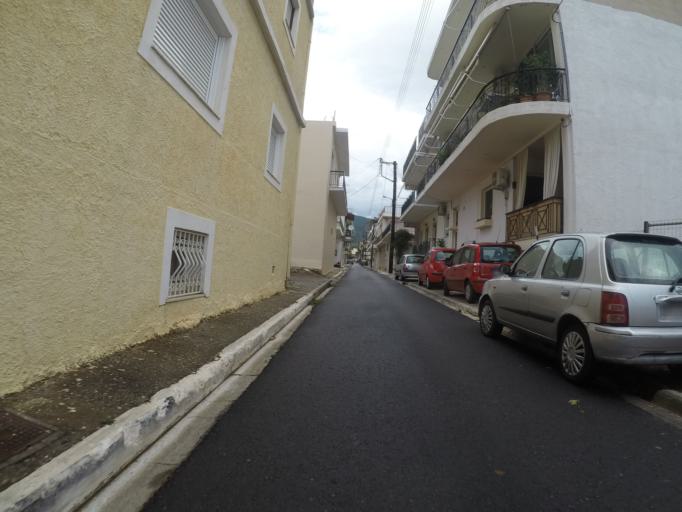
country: GR
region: Peloponnese
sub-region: Nomos Messinias
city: Kalamata
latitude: 37.0417
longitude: 22.1063
